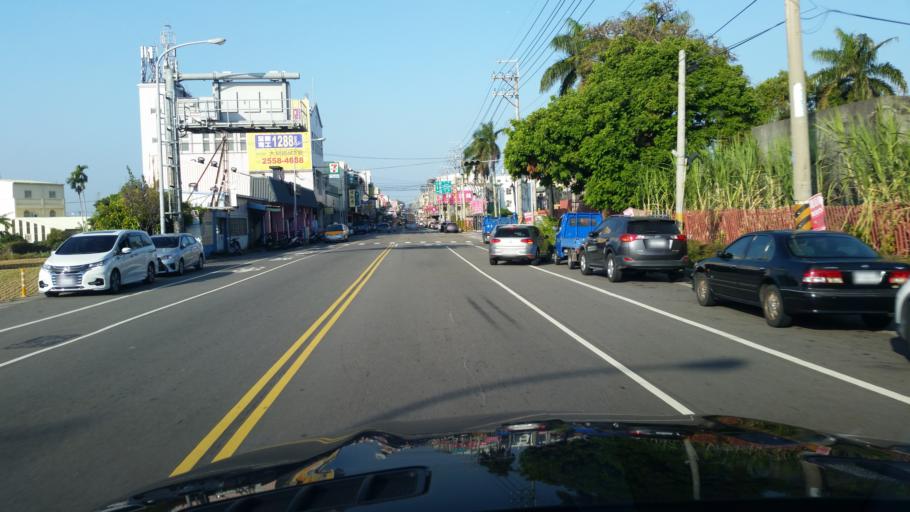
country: TW
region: Taiwan
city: Fengyuan
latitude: 24.3135
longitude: 120.6950
